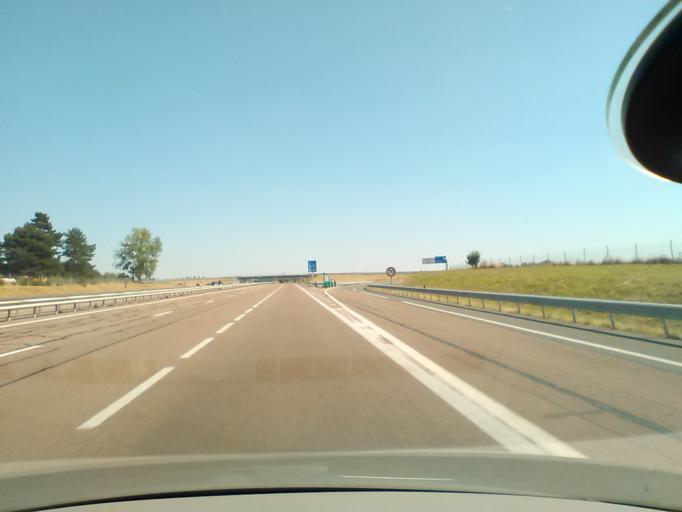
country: FR
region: Centre
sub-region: Departement du Loiret
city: Courtenay
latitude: 48.0594
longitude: 3.0914
